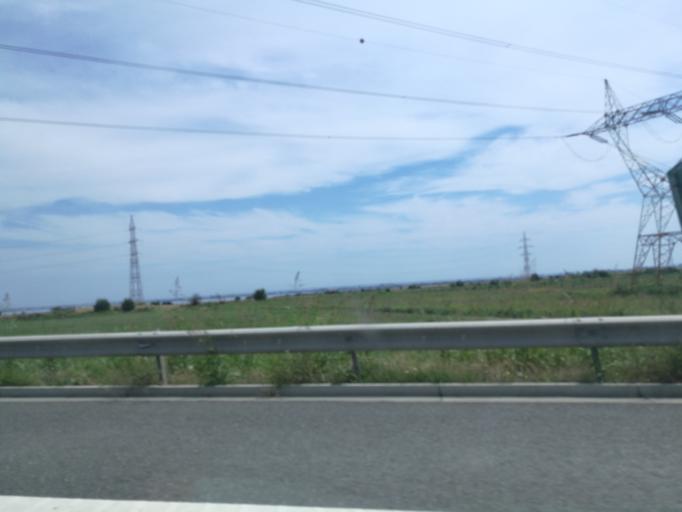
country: RO
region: Constanta
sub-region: Comuna Ovidiu
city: Ovidiu
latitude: 44.2254
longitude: 28.5509
